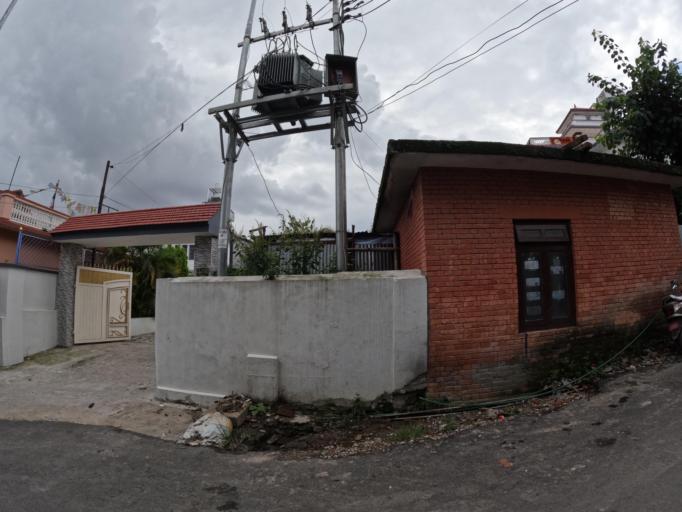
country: NP
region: Central Region
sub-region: Bagmati Zone
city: Kathmandu
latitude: 27.7409
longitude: 85.3208
